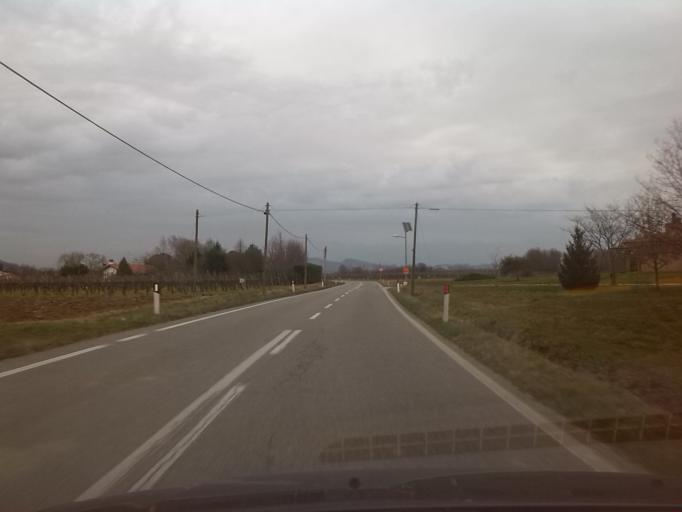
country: IT
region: Friuli Venezia Giulia
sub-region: Provincia di Gorizia
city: Romans d'Isonzo
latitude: 45.9026
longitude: 13.4410
